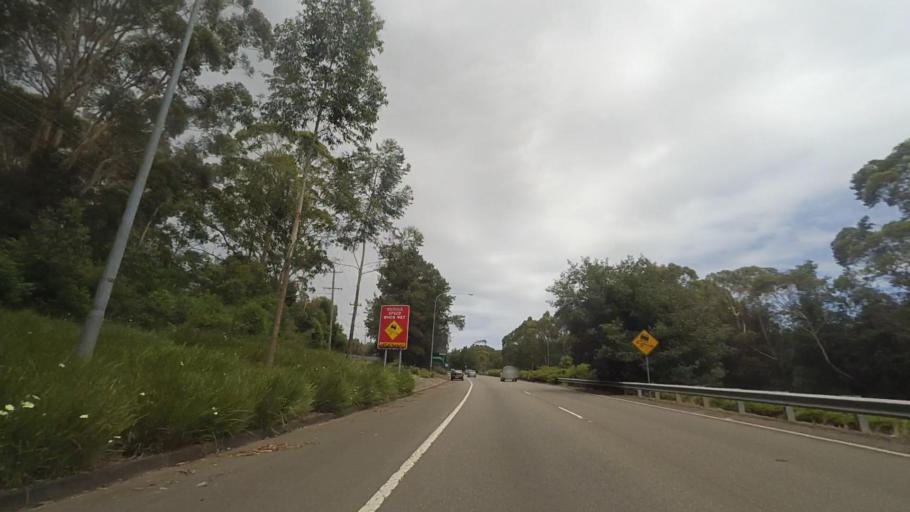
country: AU
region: New South Wales
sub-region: Wyong Shire
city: Berkeley Vale
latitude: -33.3500
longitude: 151.4321
